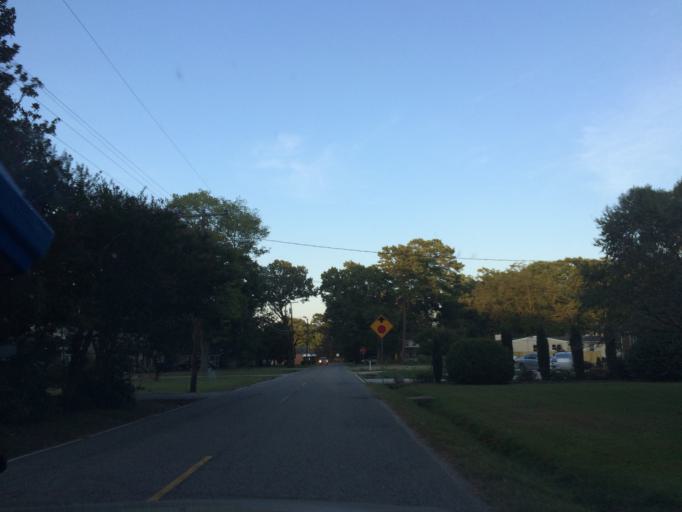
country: US
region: Virginia
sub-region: City of Newport News
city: Newport News
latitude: 37.0726
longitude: -76.4708
